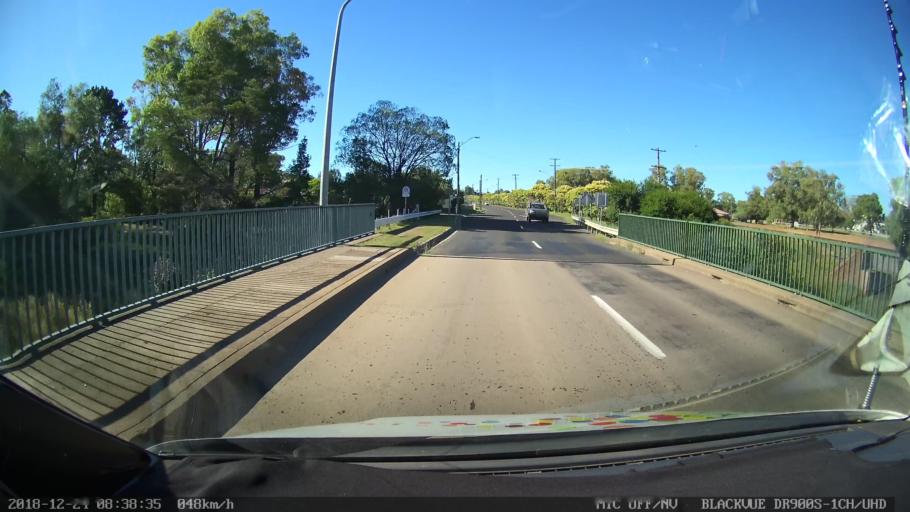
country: AU
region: New South Wales
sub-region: Liverpool Plains
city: Quirindi
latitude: -31.3419
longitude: 150.6477
